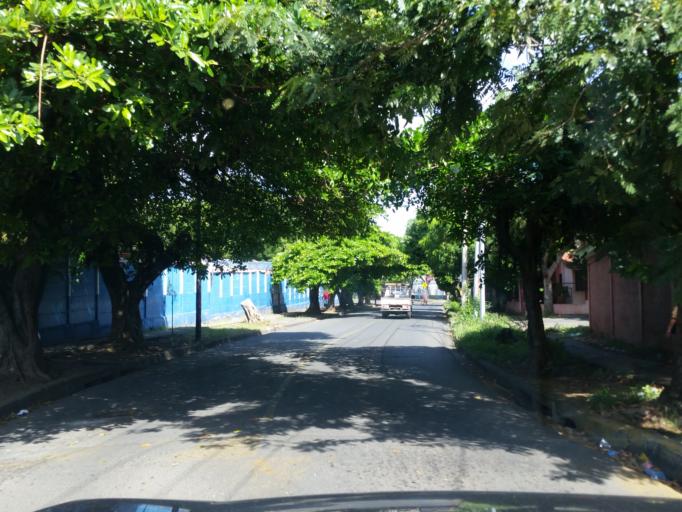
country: NI
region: Managua
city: Managua
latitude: 12.1144
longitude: -86.2491
